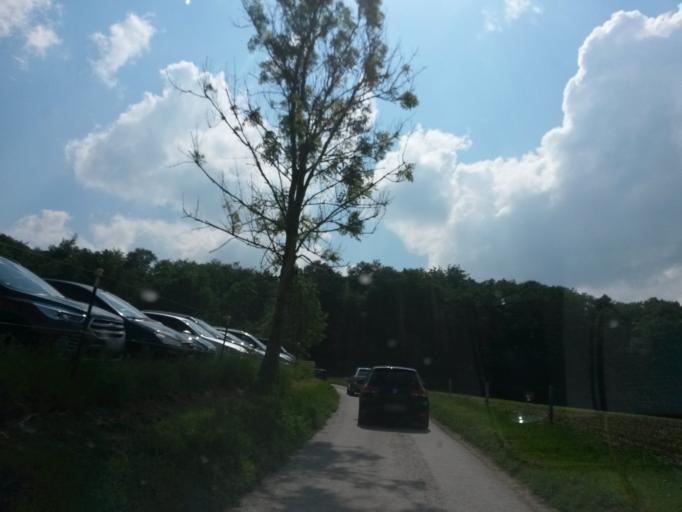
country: DE
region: North Rhine-Westphalia
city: Balve
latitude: 51.3398
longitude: 7.8888
